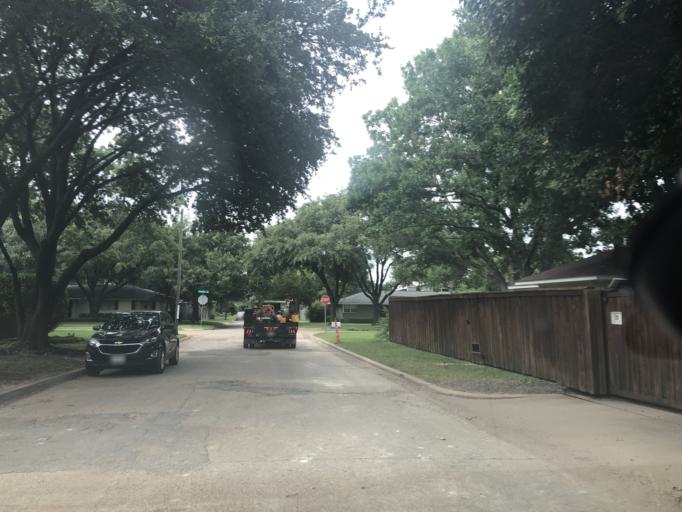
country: US
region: Texas
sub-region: Dallas County
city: University Park
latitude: 32.8704
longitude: -96.8407
